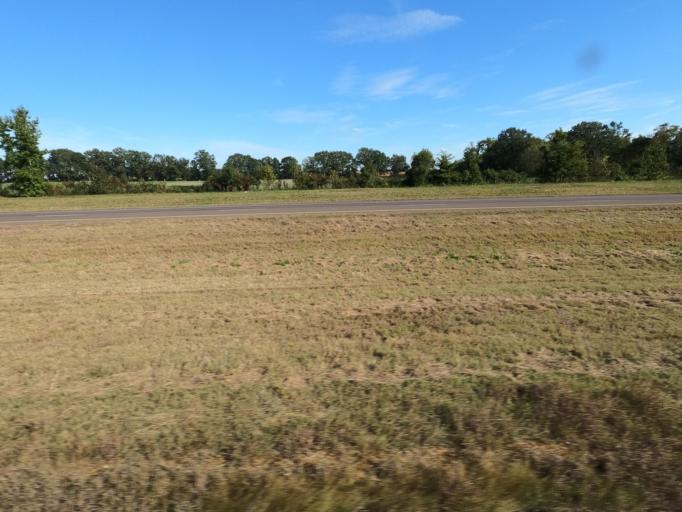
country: US
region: Tennessee
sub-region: Obion County
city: Obion
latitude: 36.2698
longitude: -89.2143
